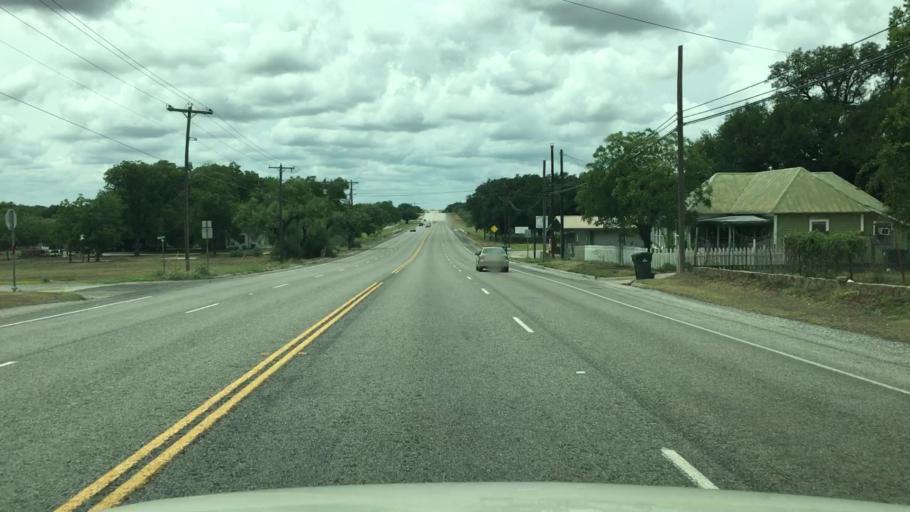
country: US
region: Texas
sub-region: Concho County
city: Eden
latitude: 31.2164
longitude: -99.8501
